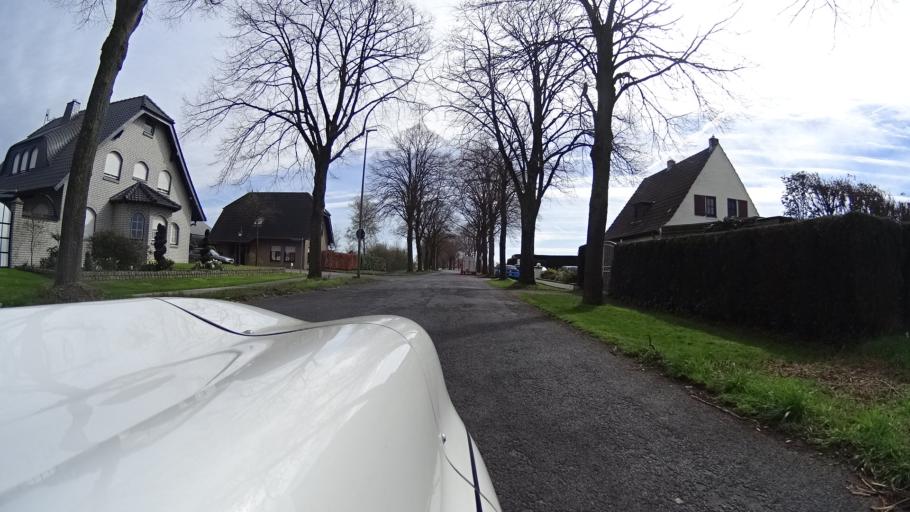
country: DE
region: North Rhine-Westphalia
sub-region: Regierungsbezirk Dusseldorf
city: Goch
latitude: 51.7046
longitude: 6.0806
